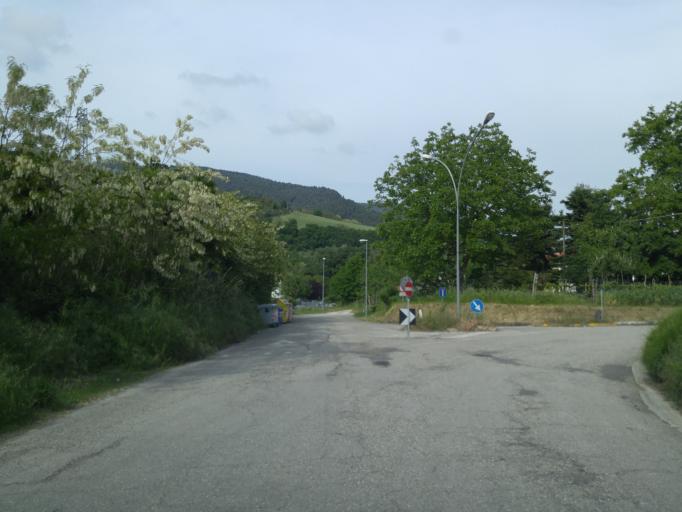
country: IT
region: The Marches
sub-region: Provincia di Pesaro e Urbino
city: Canavaccio
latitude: 43.6741
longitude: 12.7506
